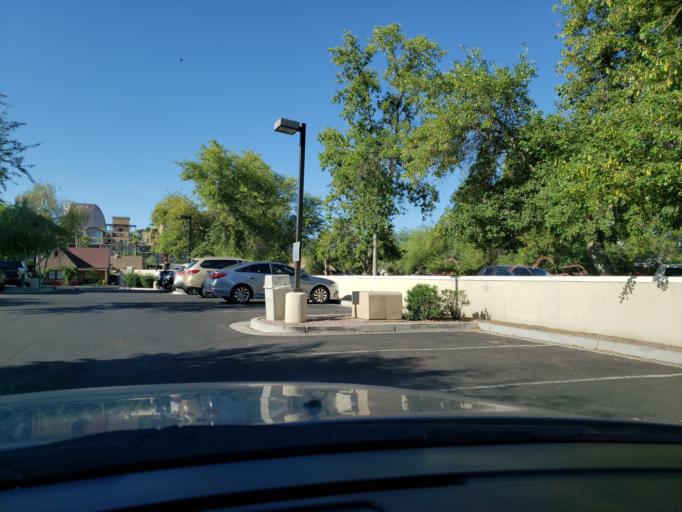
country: US
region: Arizona
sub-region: Maricopa County
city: Phoenix
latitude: 33.4764
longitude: -112.0751
